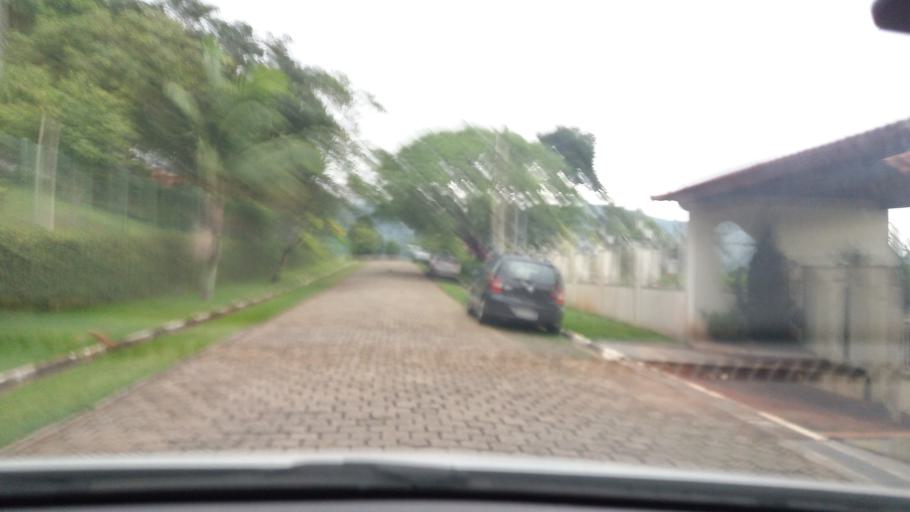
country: BR
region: Sao Paulo
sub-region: Bom Jesus Dos Perdoes
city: Bom Jesus dos Perdoes
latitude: -23.1666
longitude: -46.4635
